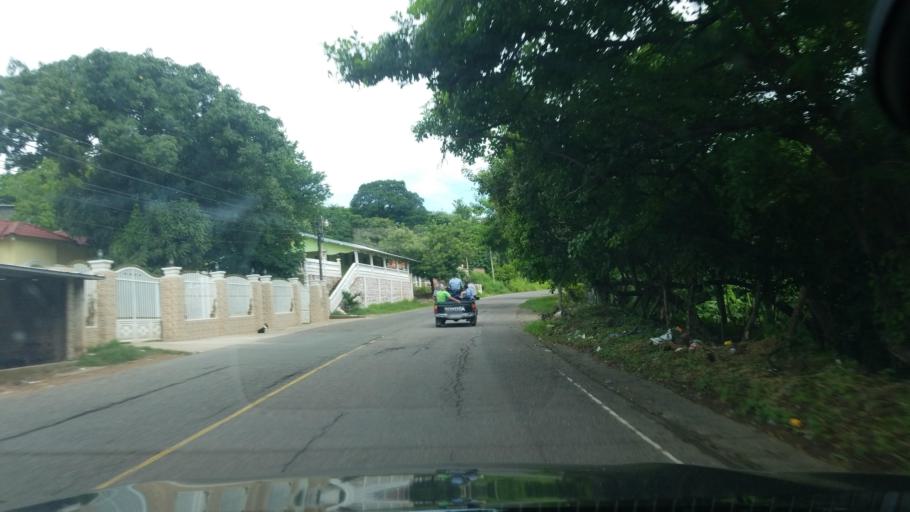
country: HN
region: Choluteca
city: Corpus
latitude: 13.3698
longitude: -87.0322
